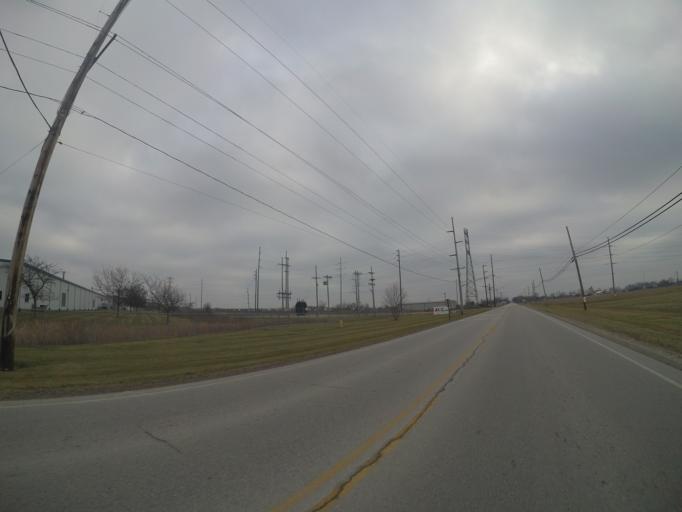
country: US
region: Ohio
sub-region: Wood County
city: Walbridge
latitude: 41.5937
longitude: -83.5125
